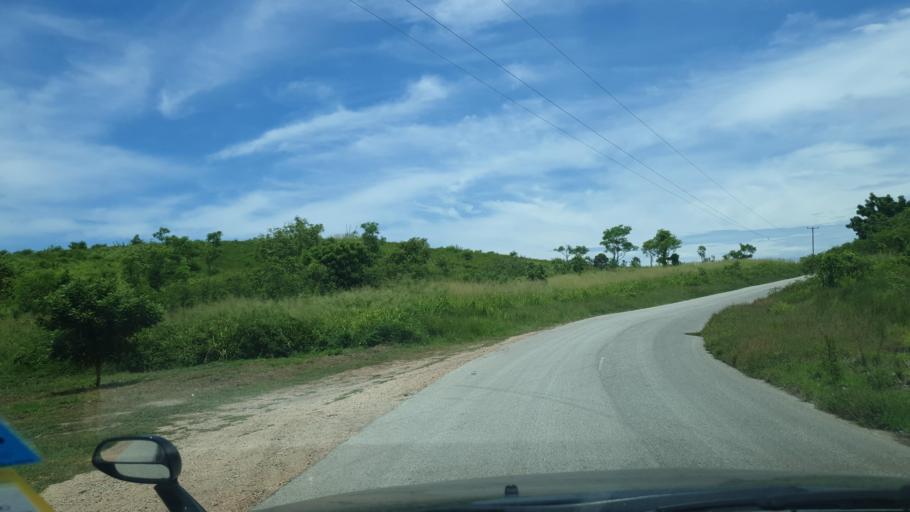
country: PG
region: National Capital
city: Port Moresby
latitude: -9.4305
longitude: 147.0548
